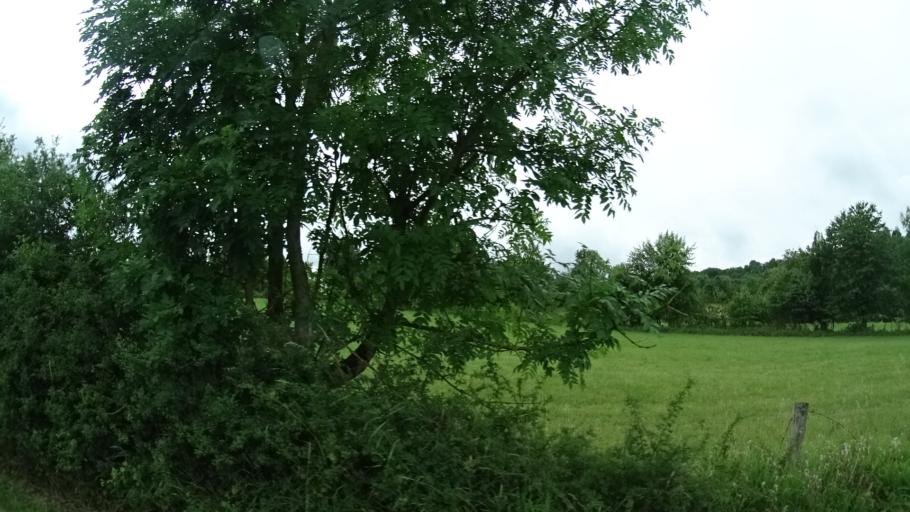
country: DE
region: Saarland
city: Mettlach
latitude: 49.4466
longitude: 6.5877
